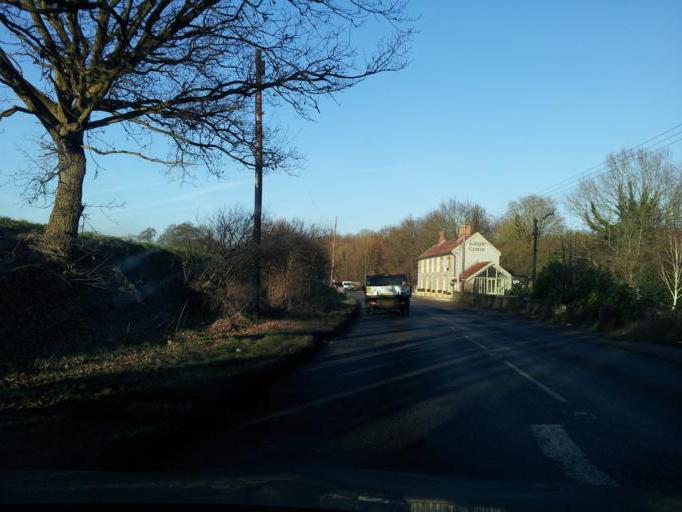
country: GB
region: England
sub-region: Suffolk
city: Bury St Edmunds
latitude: 52.2049
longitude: 0.7562
